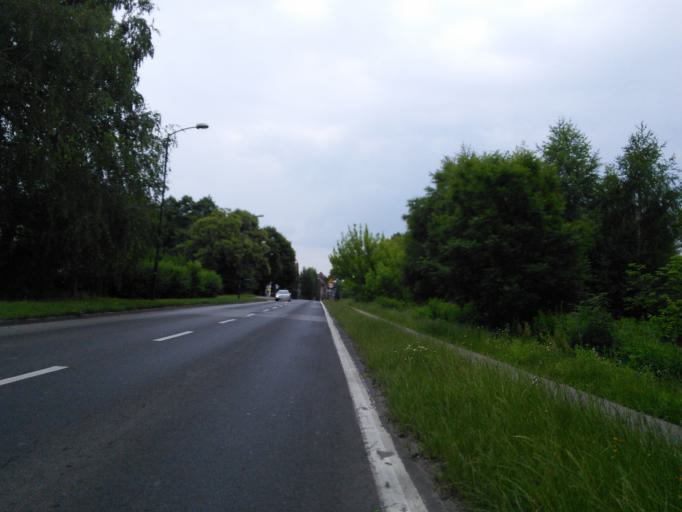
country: PL
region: Silesian Voivodeship
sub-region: Piekary Slaskie
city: Brzeziny Slaskie
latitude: 50.3701
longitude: 18.9688
